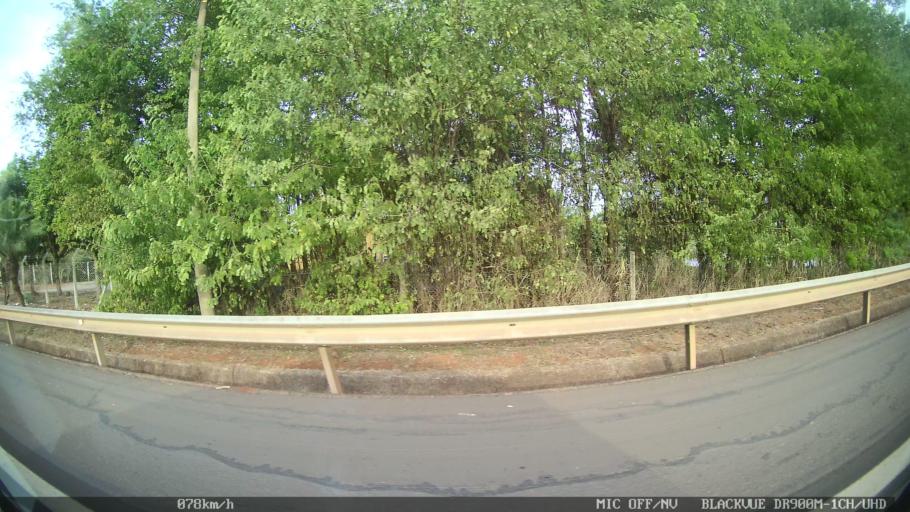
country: BR
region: Sao Paulo
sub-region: Iracemapolis
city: Iracemapolis
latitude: -22.5944
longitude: -47.4662
